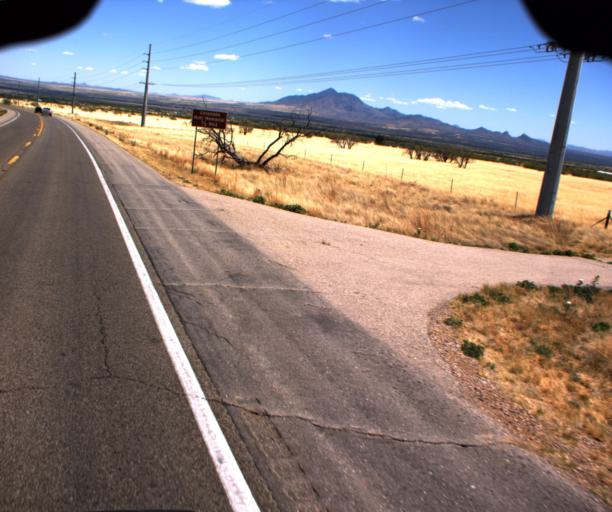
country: US
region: Arizona
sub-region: Cochise County
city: Sierra Vista Southeast
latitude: 31.3802
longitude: -110.2156
